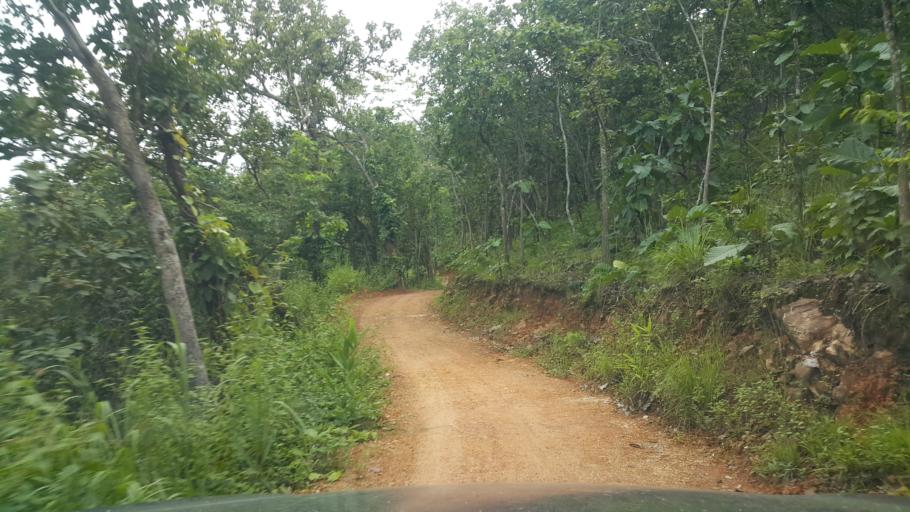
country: TH
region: Chiang Mai
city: San Sai
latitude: 18.9656
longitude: 99.1276
